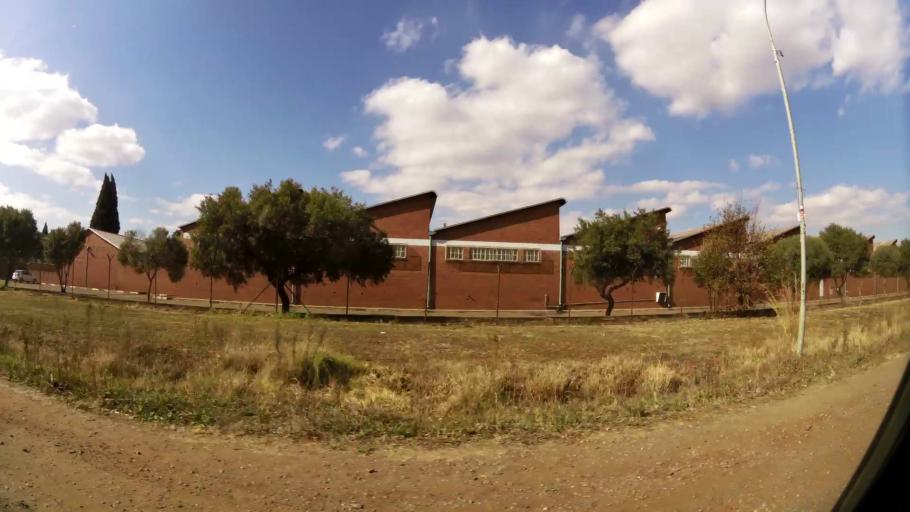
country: ZA
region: Gauteng
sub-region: Ekurhuleni Metropolitan Municipality
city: Tembisa
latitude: -25.9806
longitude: 28.2449
